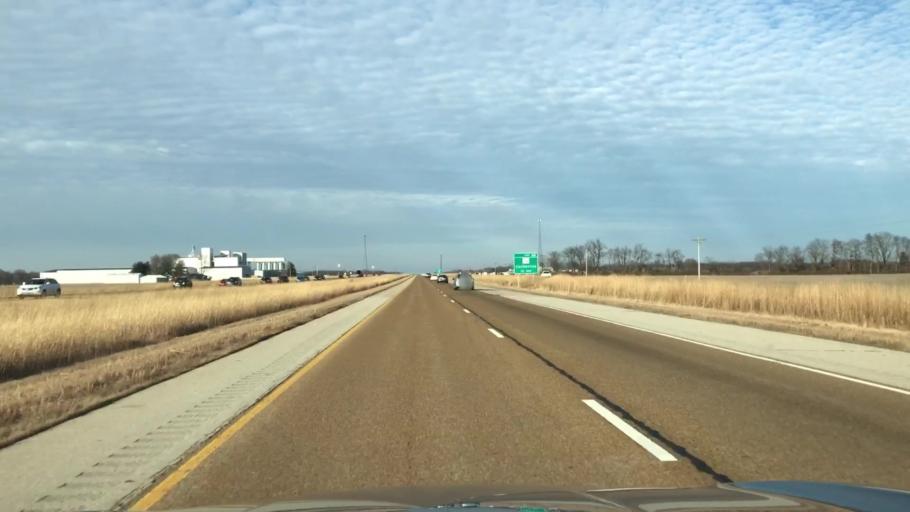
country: US
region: Illinois
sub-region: Montgomery County
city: Raymond
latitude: 39.2652
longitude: -89.6411
